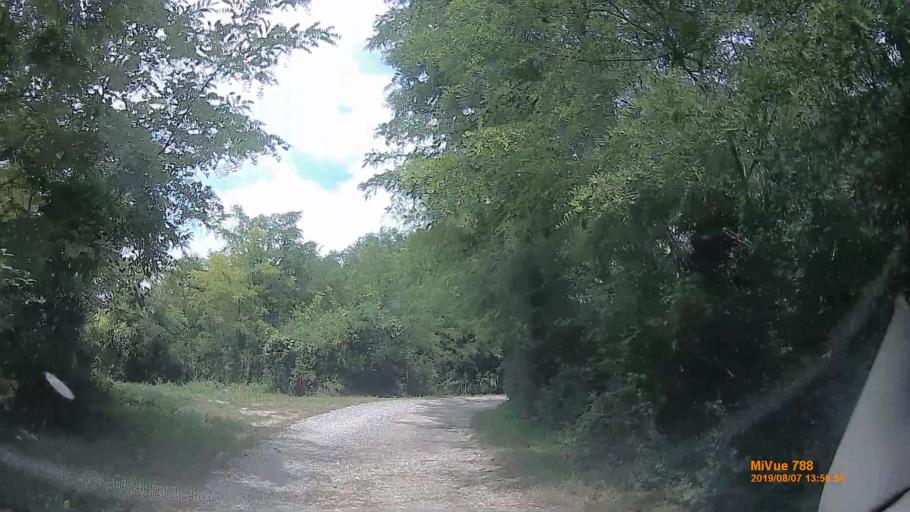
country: HU
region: Zala
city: Cserszegtomaj
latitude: 46.8947
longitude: 17.1760
